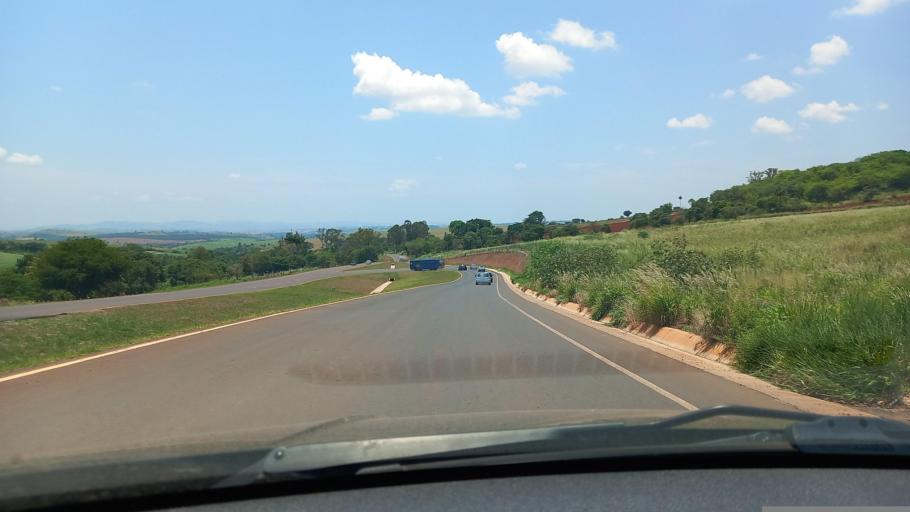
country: BR
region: Sao Paulo
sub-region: Moji-Guacu
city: Mogi-Gaucu
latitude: -22.3382
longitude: -46.8825
